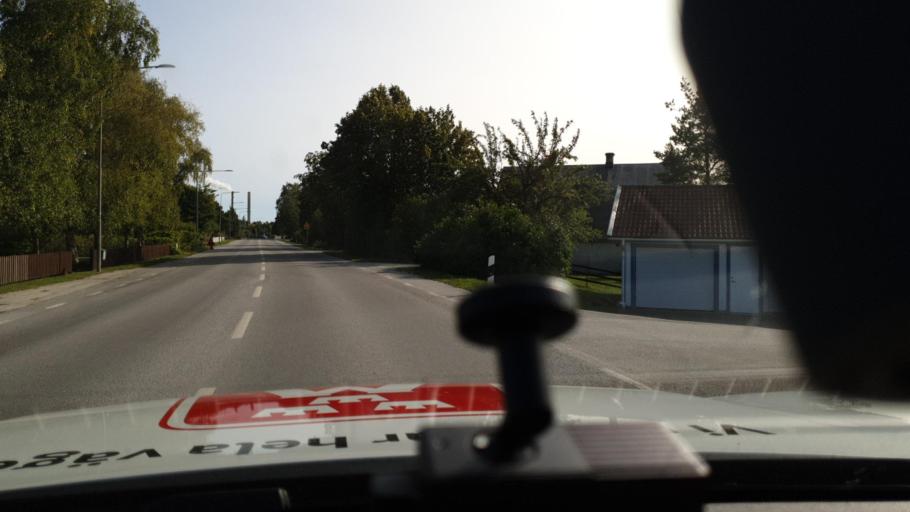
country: SE
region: Gotland
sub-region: Gotland
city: Slite
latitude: 57.7230
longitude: 18.7885
